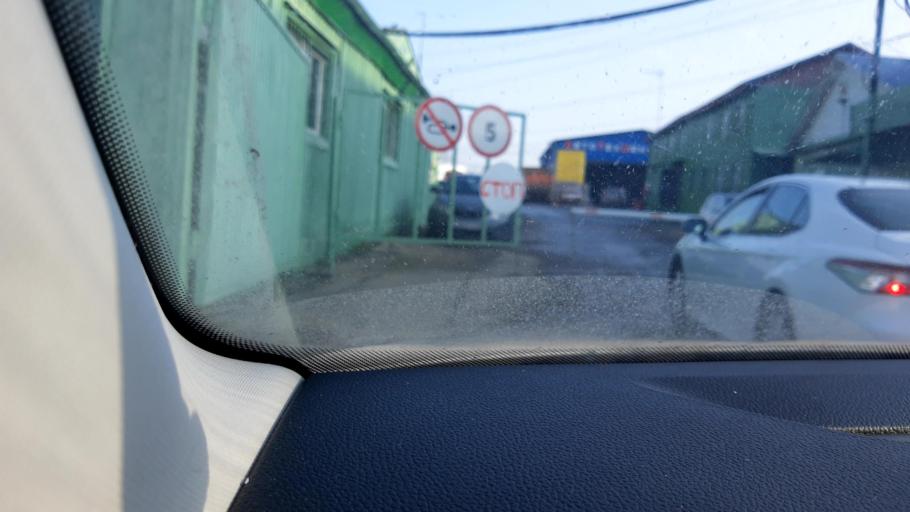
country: RU
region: Moscow
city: Annino
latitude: 55.5735
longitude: 37.6190
